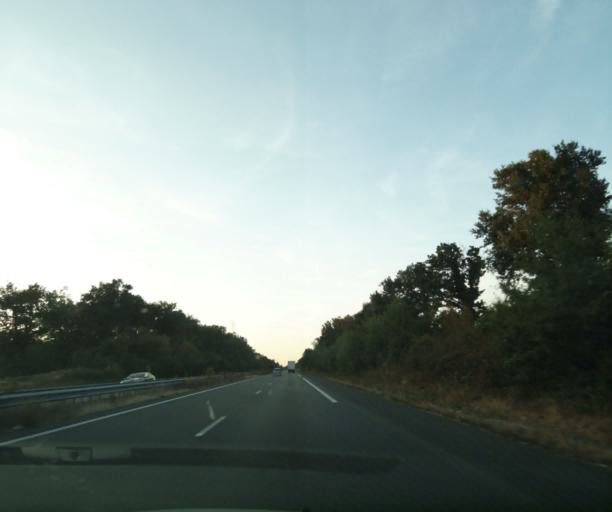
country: FR
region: Aquitaine
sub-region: Departement du Lot-et-Garonne
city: Fourques-sur-Garonne
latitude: 44.4036
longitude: 0.1869
